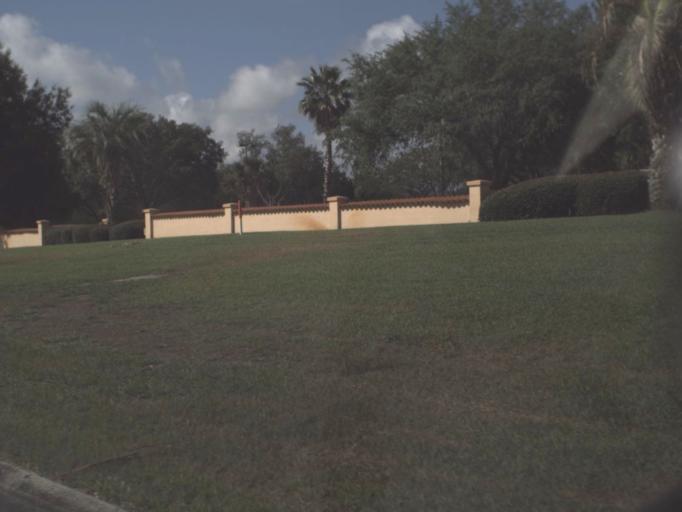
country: US
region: Florida
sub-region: Sumter County
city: The Villages
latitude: 28.9475
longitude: -81.9527
